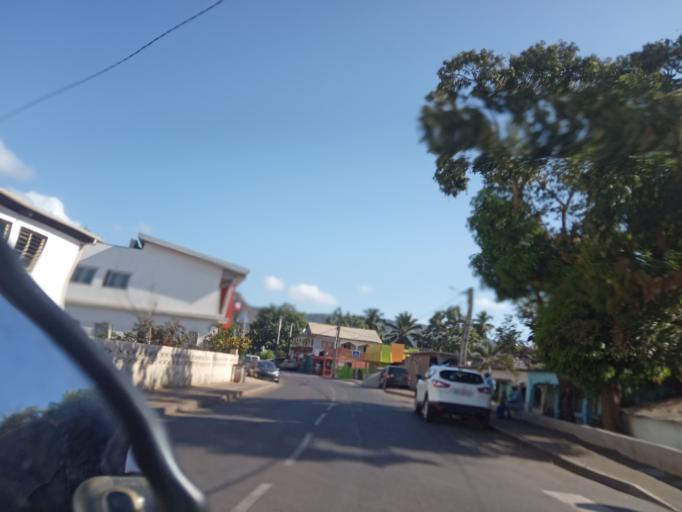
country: YT
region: Bandrele
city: Bandrele
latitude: -12.9113
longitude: 45.1929
